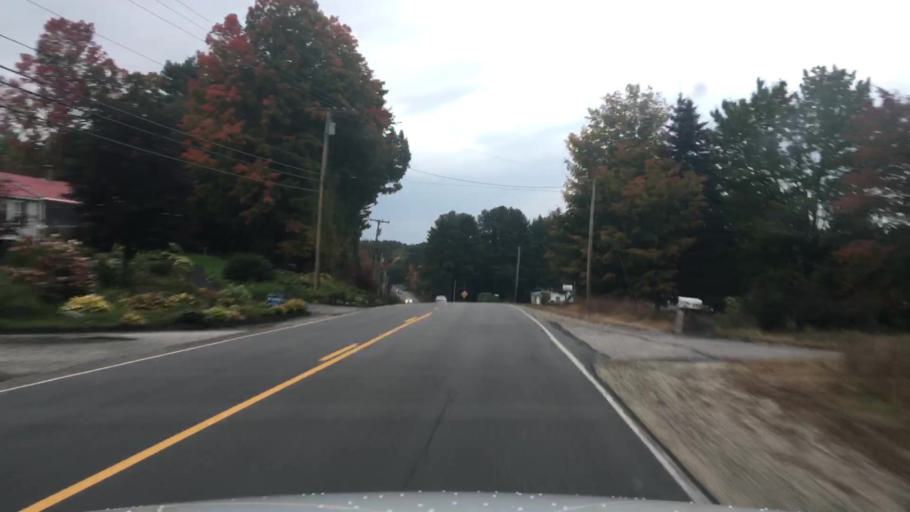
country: US
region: Maine
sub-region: York County
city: Hollis Center
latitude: 43.6073
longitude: -70.5799
